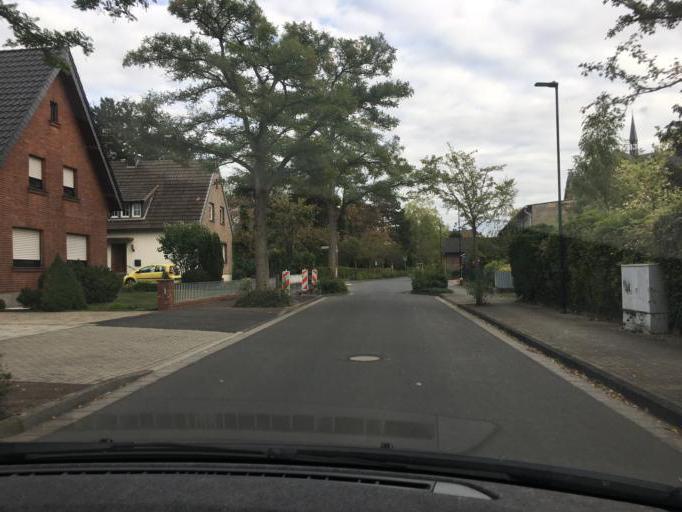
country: DE
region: North Rhine-Westphalia
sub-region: Regierungsbezirk Koln
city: Merzenich
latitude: 50.8612
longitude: 6.5813
